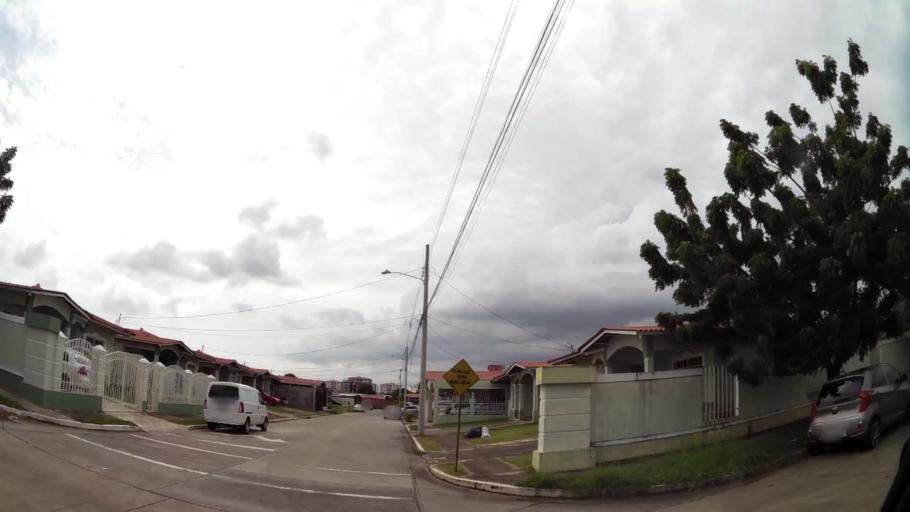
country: PA
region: Panama
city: Tocumen
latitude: 9.0445
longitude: -79.4127
